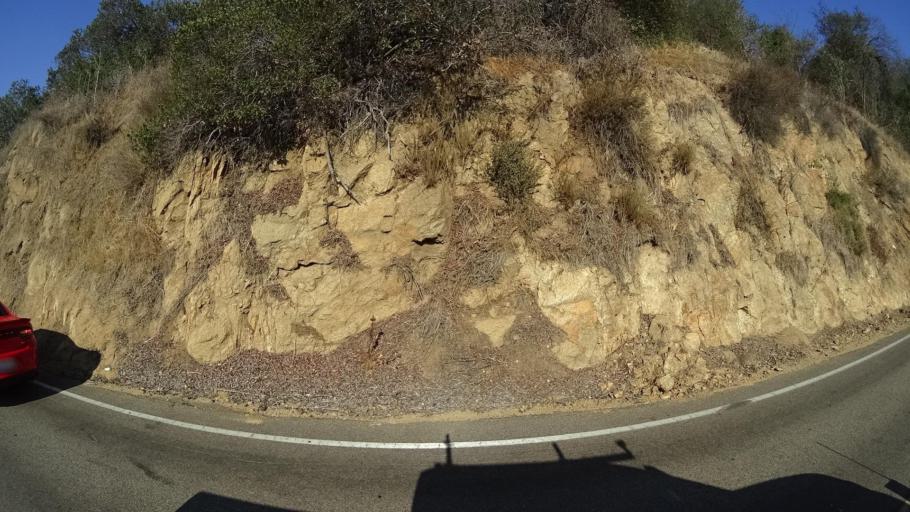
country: US
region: California
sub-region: San Diego County
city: Bonsall
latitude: 33.2955
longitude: -117.2427
